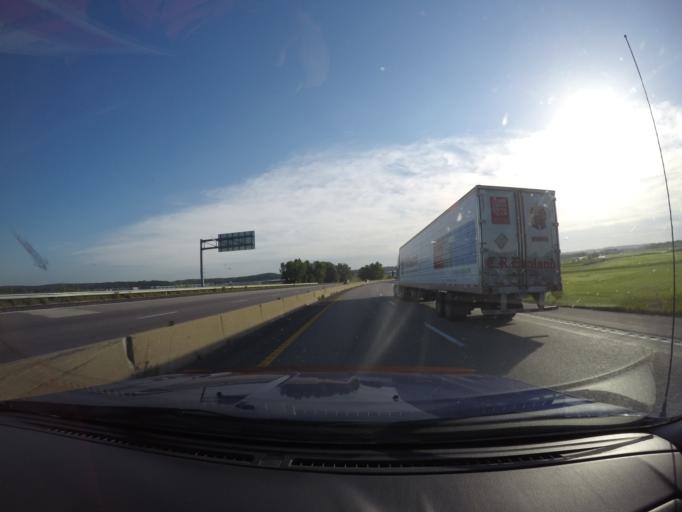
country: US
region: Missouri
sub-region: Platte County
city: Riverside
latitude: 39.1576
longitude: -94.6484
